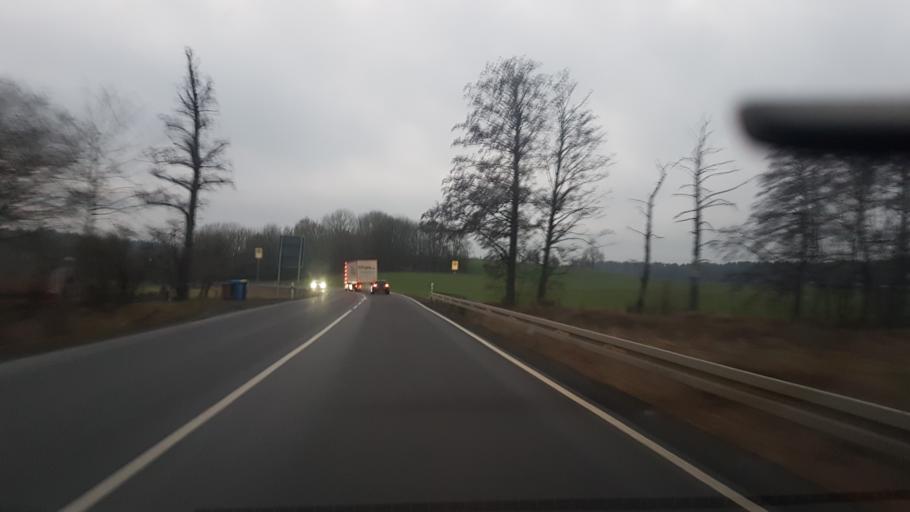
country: DE
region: Bavaria
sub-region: Regierungsbezirk Unterfranken
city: Maroldsweisach
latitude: 50.1822
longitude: 10.6778
